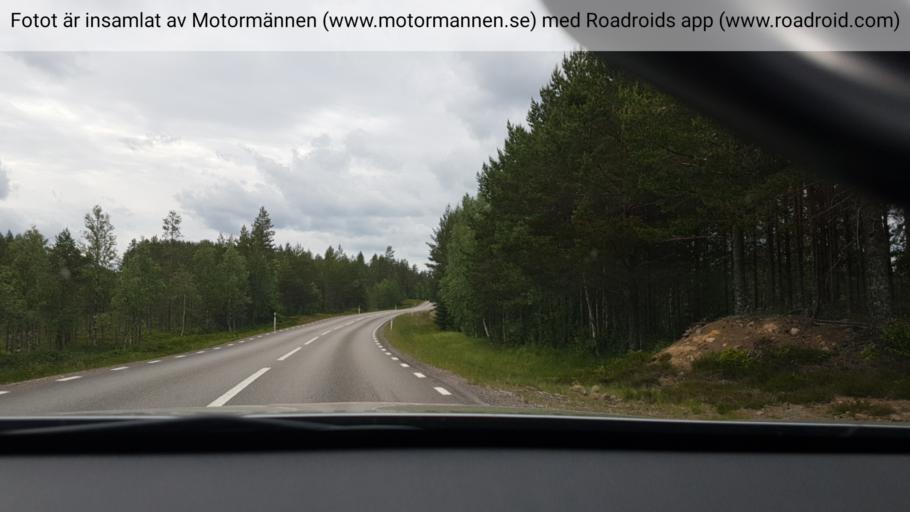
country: SE
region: Vaermland
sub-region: Torsby Kommun
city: Torsby
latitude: 60.3675
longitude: 13.1978
